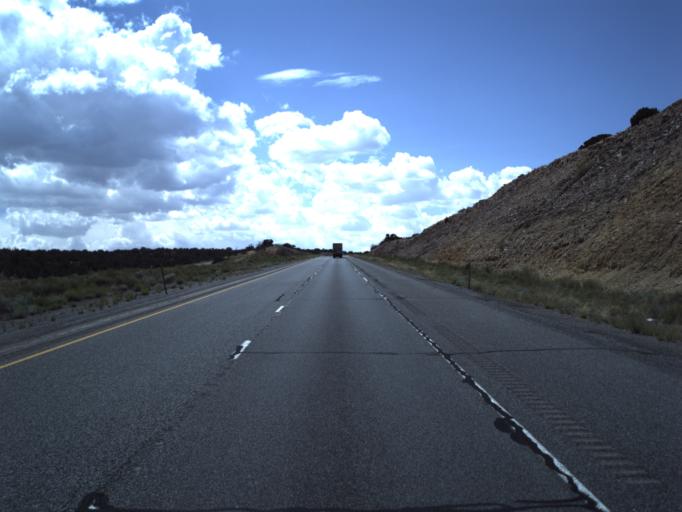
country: US
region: Utah
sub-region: Emery County
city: Castle Dale
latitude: 38.9009
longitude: -110.5693
